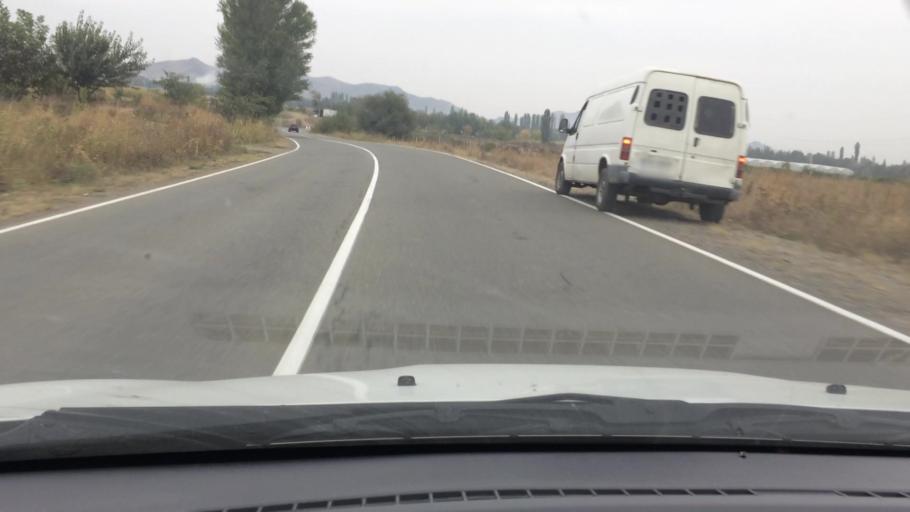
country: GE
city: Naghvarevi
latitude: 41.3140
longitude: 44.7933
